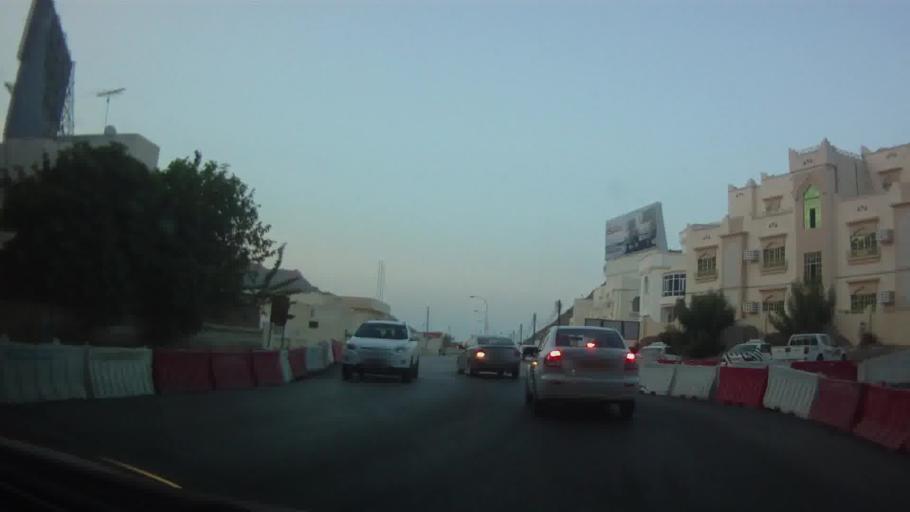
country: OM
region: Muhafazat Masqat
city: Muscat
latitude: 23.6197
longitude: 58.5404
